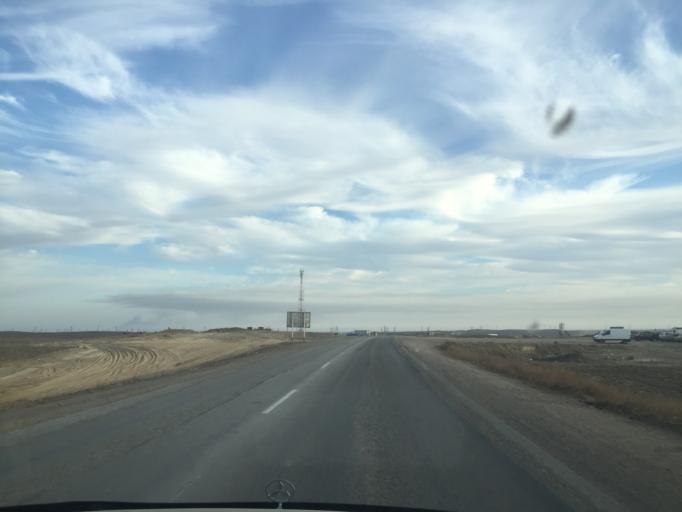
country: KZ
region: Almaty Oblysy
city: Ulken
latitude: 45.1630
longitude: 73.9416
